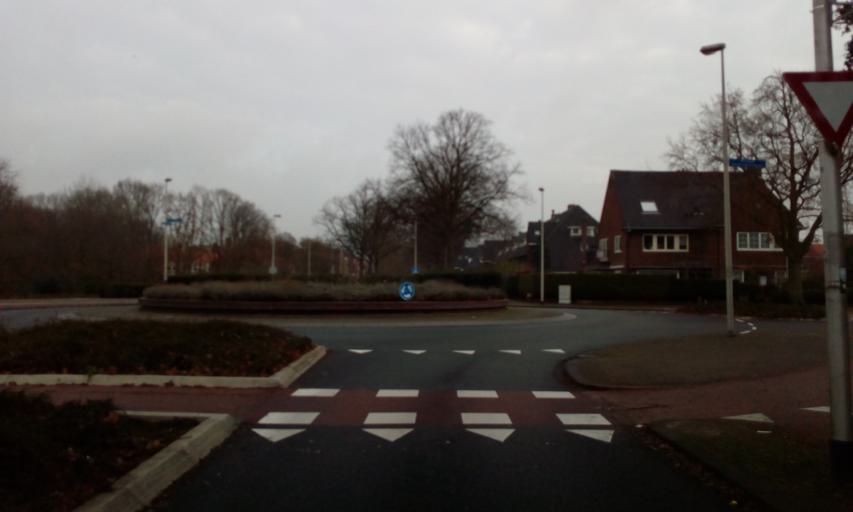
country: NL
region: North Holland
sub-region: Gemeente Bussum
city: Bussum
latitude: 52.2754
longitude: 5.1740
